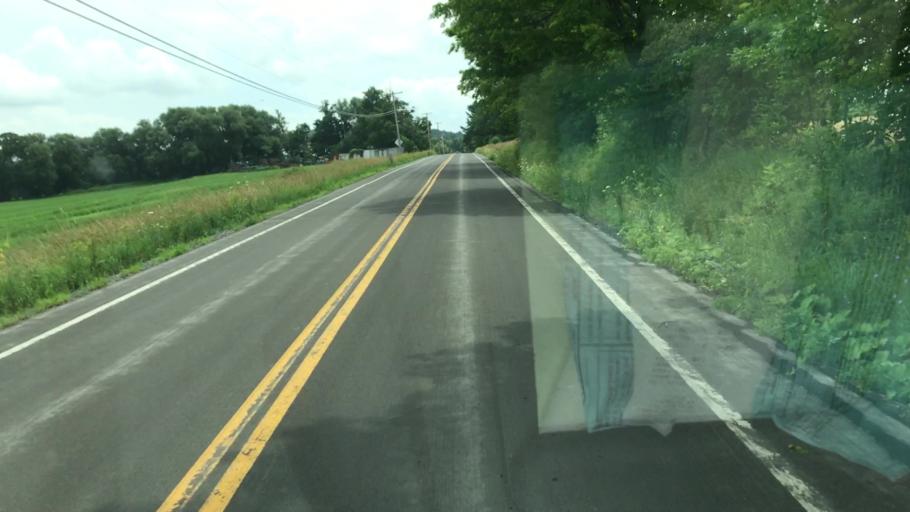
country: US
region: New York
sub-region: Onondaga County
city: Manlius
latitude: 42.9262
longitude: -75.9762
